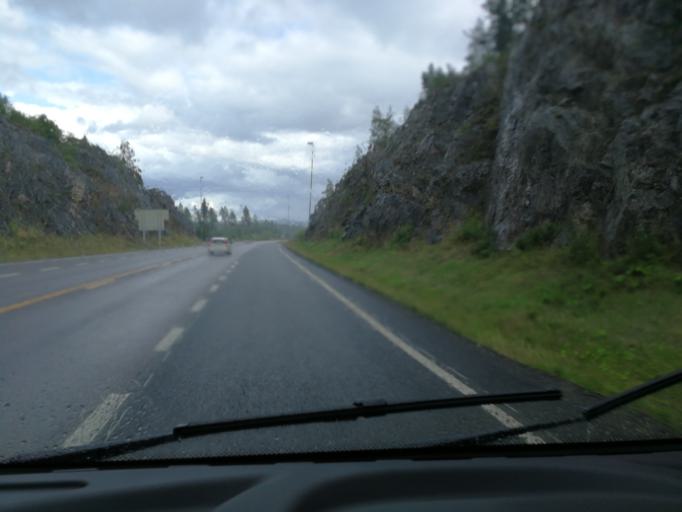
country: NO
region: Ostfold
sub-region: Marker
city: Orje
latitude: 59.5394
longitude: 11.5416
